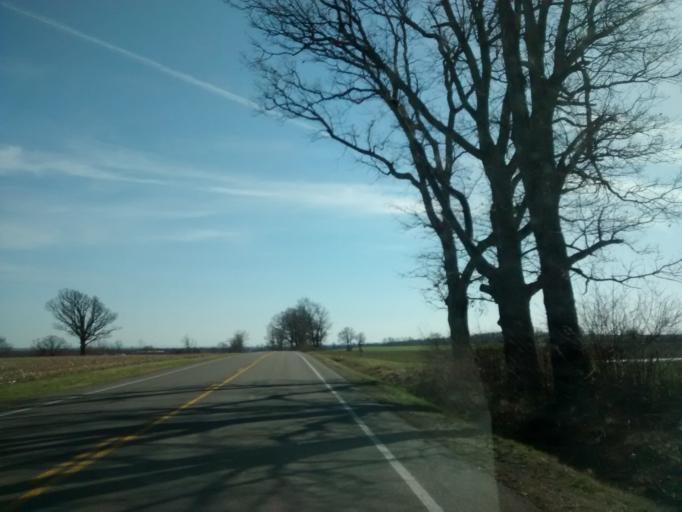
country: US
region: New York
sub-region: Livingston County
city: Avon
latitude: 42.9574
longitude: -77.7660
